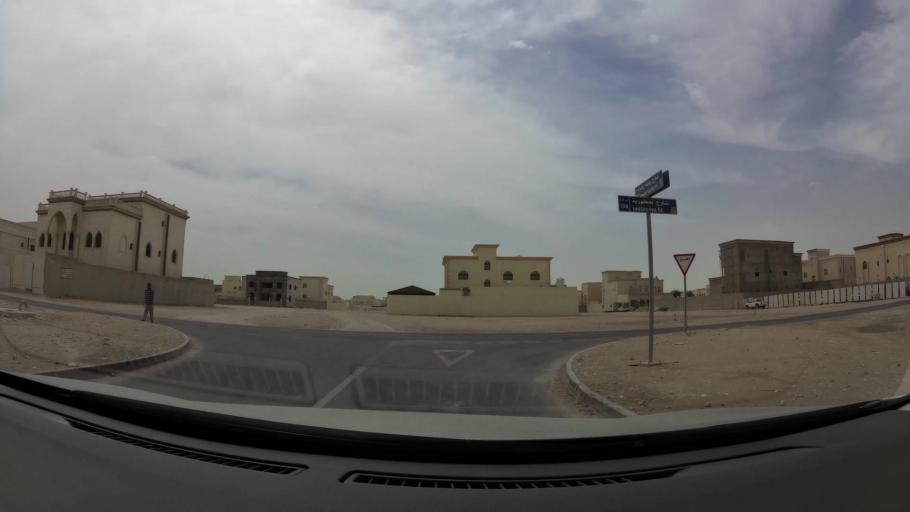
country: QA
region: Baladiyat ad Dawhah
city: Doha
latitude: 25.2117
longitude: 51.4668
